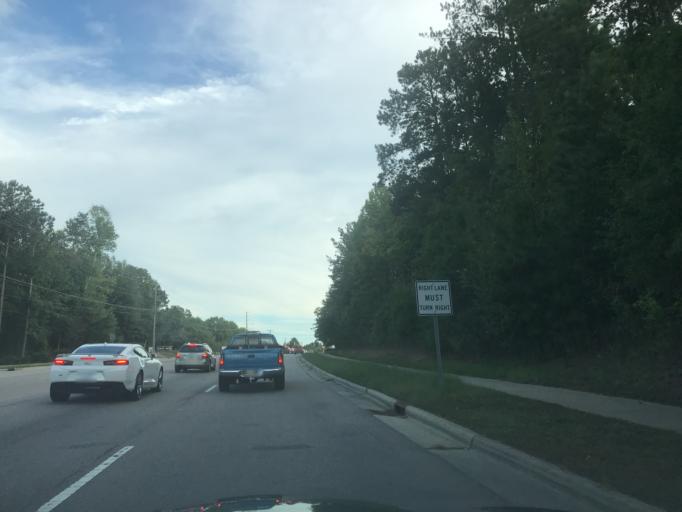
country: US
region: North Carolina
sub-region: Wake County
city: Apex
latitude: 35.7375
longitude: -78.8642
